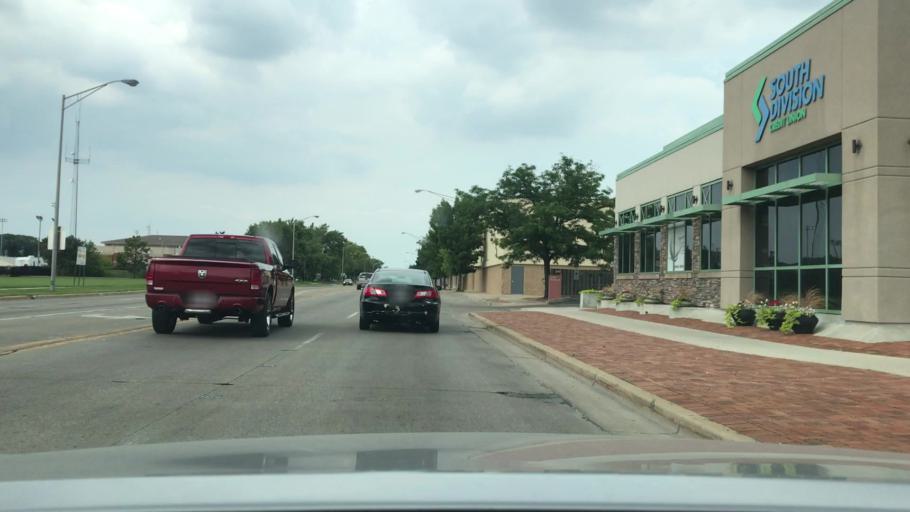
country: US
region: Illinois
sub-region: Cook County
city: Evergreen Park
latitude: 41.7282
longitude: -87.7020
